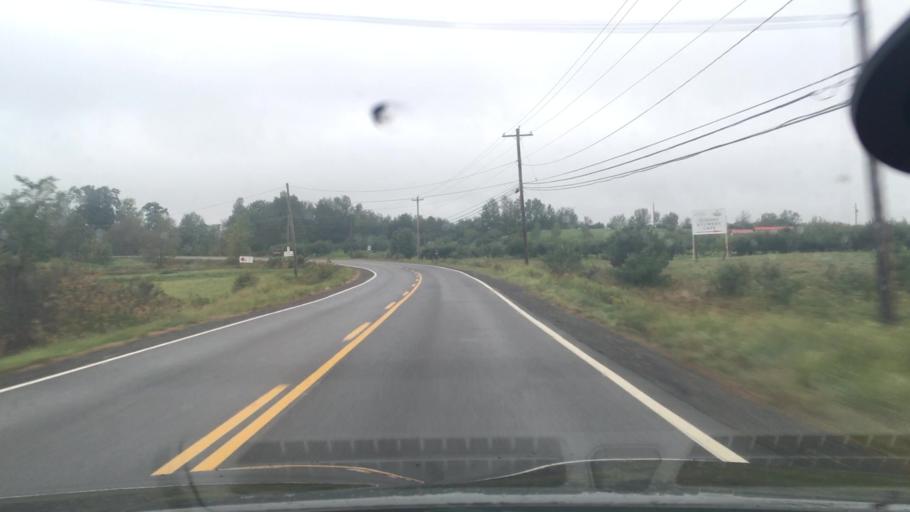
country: CA
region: Nova Scotia
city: Windsor
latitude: 44.9505
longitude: -64.1715
